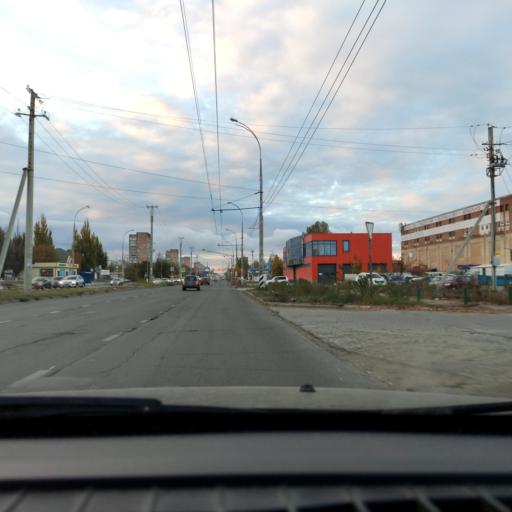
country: RU
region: Samara
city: Tol'yatti
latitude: 53.5403
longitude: 49.3000
